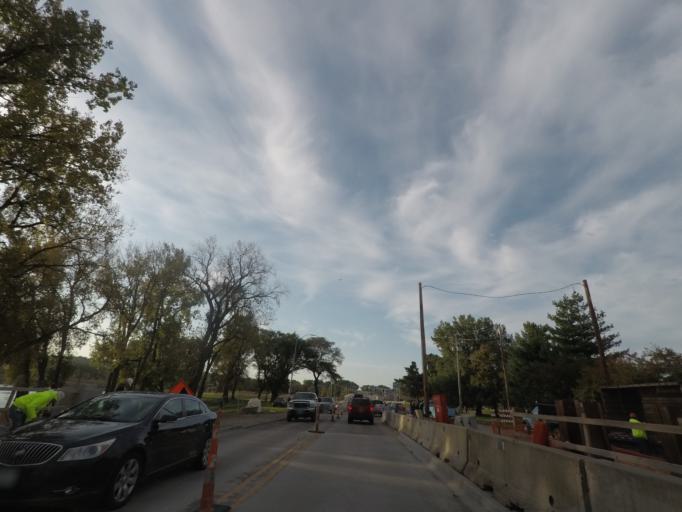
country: US
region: Iowa
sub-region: Polk County
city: Des Moines
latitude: 41.5700
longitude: -93.6449
